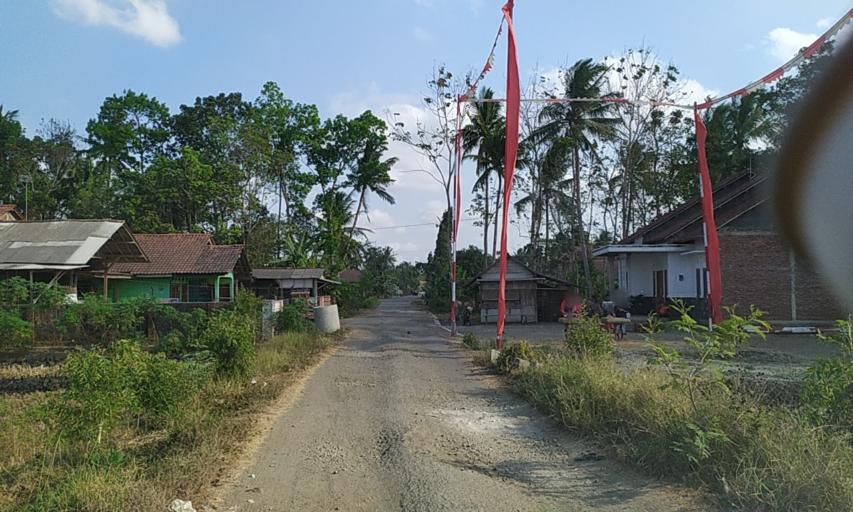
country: ID
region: Central Java
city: Wanadadi
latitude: -7.5317
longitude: 108.8205
